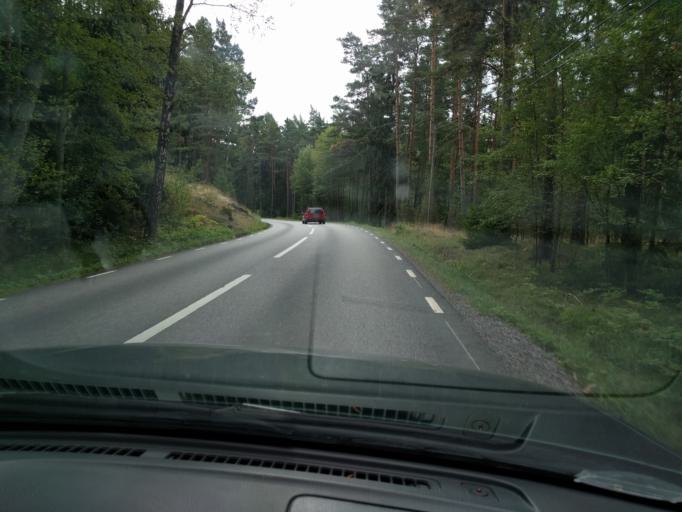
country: SE
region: Soedermanland
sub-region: Nykopings Kommun
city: Svalsta
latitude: 58.5220
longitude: 16.7718
